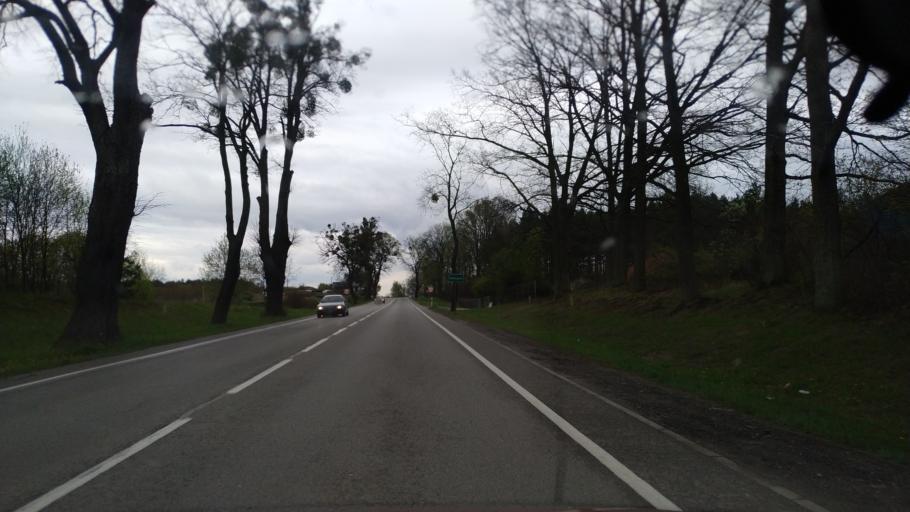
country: PL
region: Pomeranian Voivodeship
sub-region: Powiat tczewski
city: Pelplin
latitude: 54.0204
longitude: 18.6323
